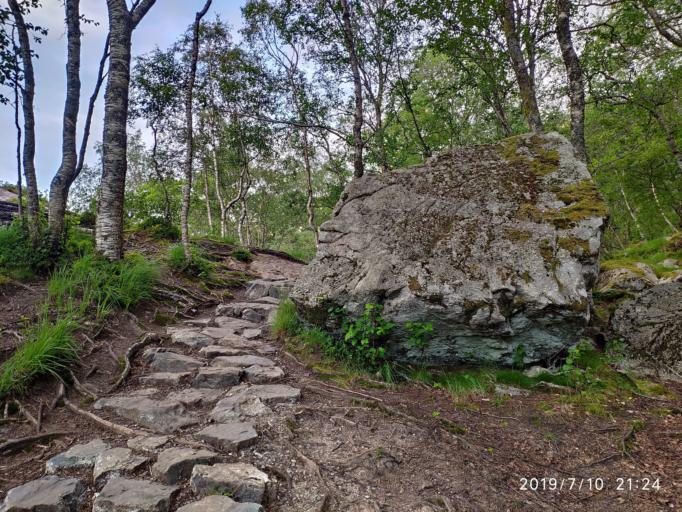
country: NO
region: Rogaland
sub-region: Forsand
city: Forsand
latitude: 58.8564
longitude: 6.3857
